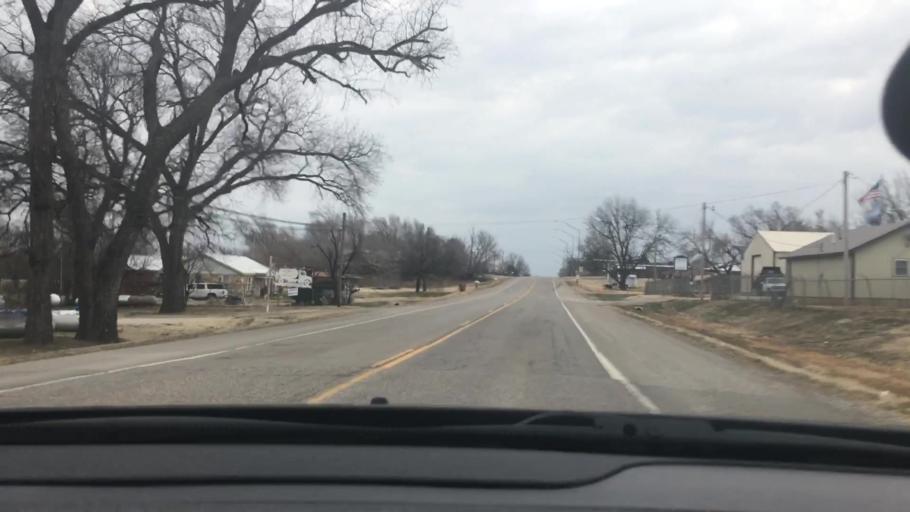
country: US
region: Oklahoma
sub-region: Garvin County
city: Maysville
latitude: 34.8176
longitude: -97.4226
